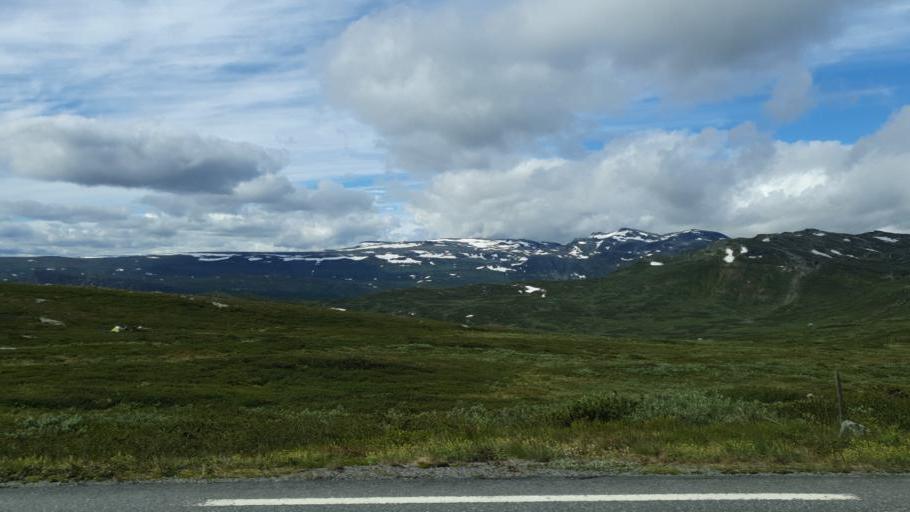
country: NO
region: Oppland
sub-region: Vestre Slidre
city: Slidre
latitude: 61.2848
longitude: 8.8283
